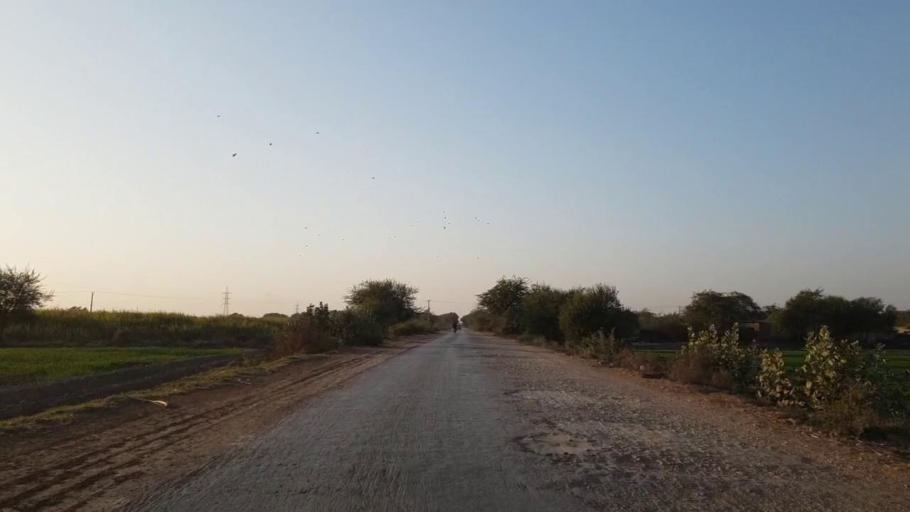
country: PK
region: Sindh
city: Chambar
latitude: 25.2320
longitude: 68.7043
